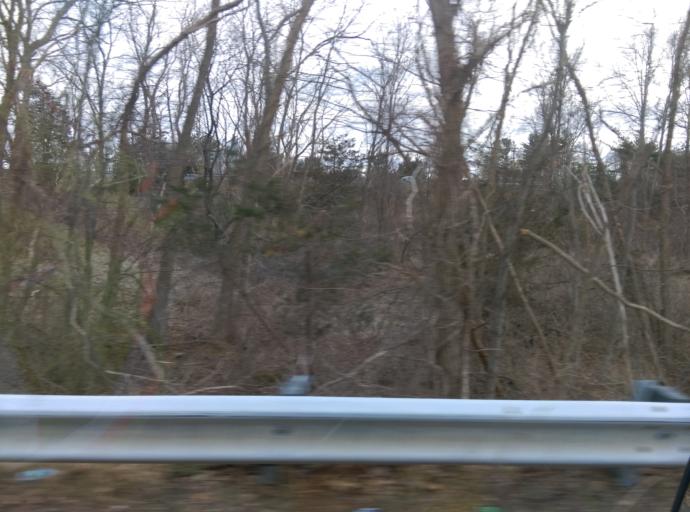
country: US
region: Massachusetts
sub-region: Essex County
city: Amesbury
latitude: 42.8407
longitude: -70.9357
